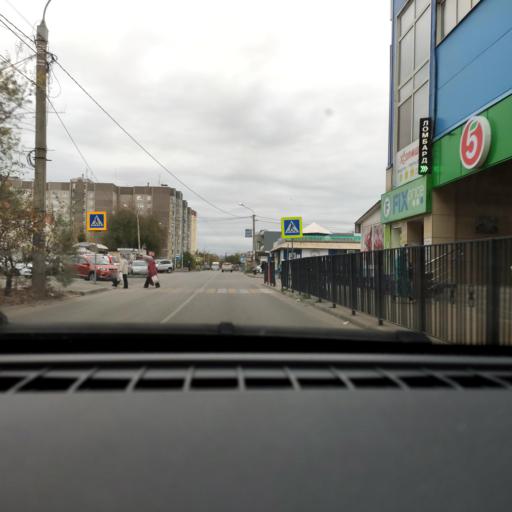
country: RU
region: Voronezj
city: Somovo
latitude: 51.7369
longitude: 39.2913
